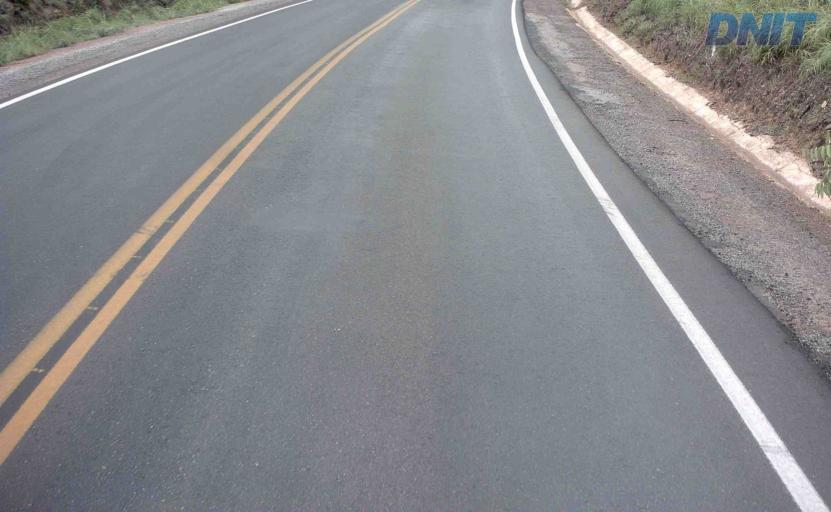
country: BR
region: Goias
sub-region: Padre Bernardo
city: Padre Bernardo
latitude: -15.4621
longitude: -48.2179
